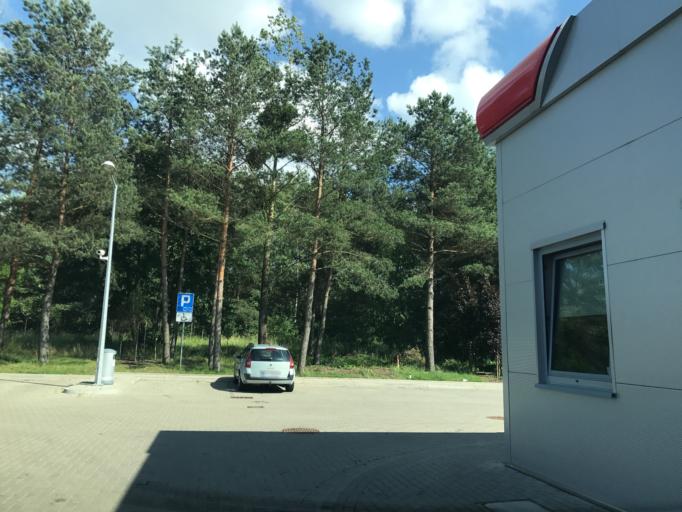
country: PL
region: Warmian-Masurian Voivodeship
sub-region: Powiat ilawski
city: Ilawa
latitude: 53.5782
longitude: 19.5883
